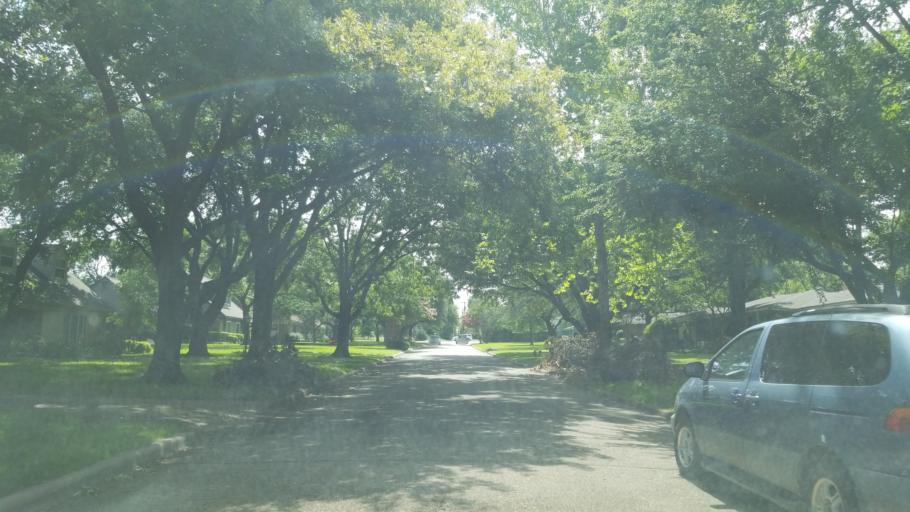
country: US
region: Texas
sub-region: Dallas County
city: Addison
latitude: 32.9049
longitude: -96.8401
